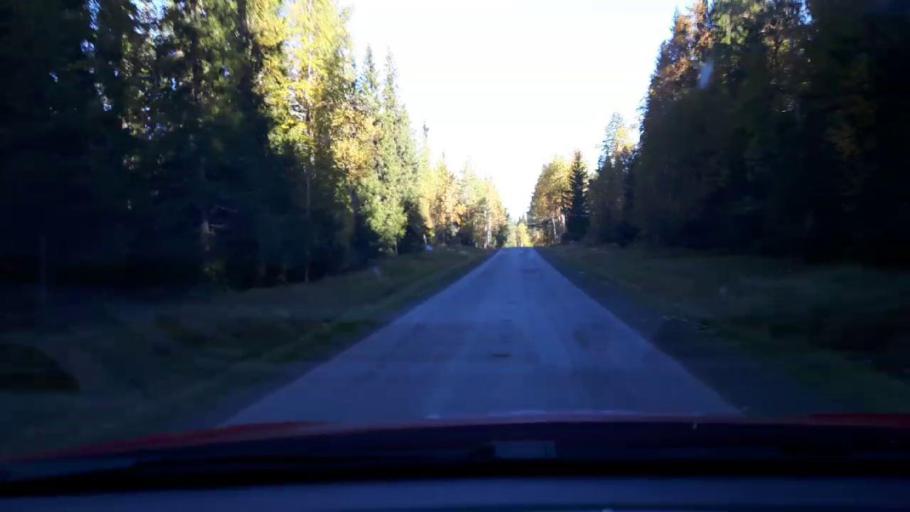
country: SE
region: Jaemtland
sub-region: Stroemsunds Kommun
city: Stroemsund
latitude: 64.3959
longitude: 15.1470
